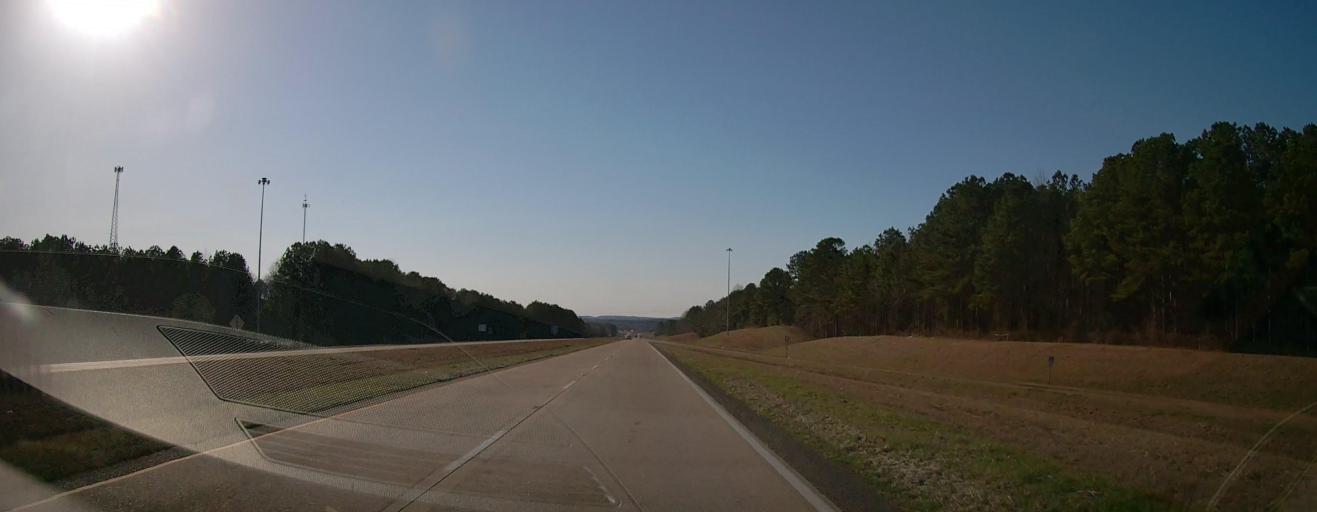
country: US
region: Mississippi
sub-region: Tishomingo County
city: Iuka
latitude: 34.7941
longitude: -88.2111
